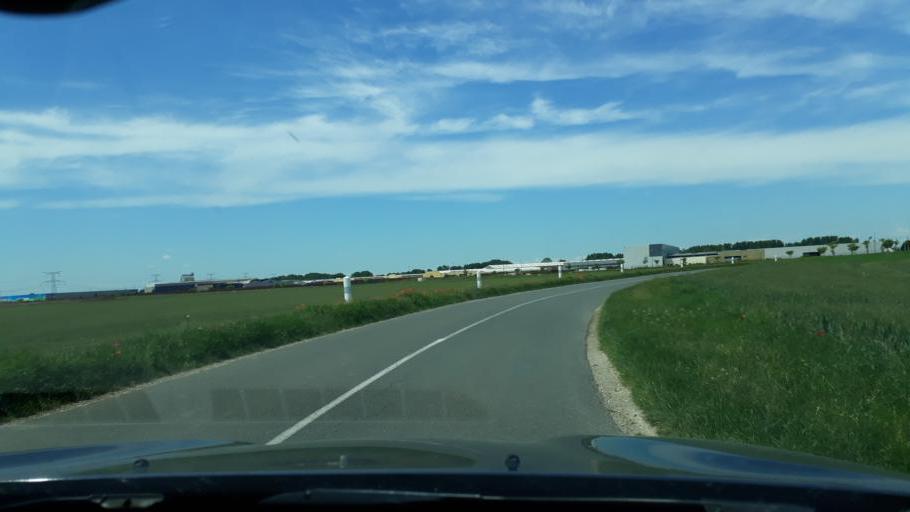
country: FR
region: Centre
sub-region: Departement du Loiret
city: Pithiviers-le-Vieil
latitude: 48.1241
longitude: 2.2015
